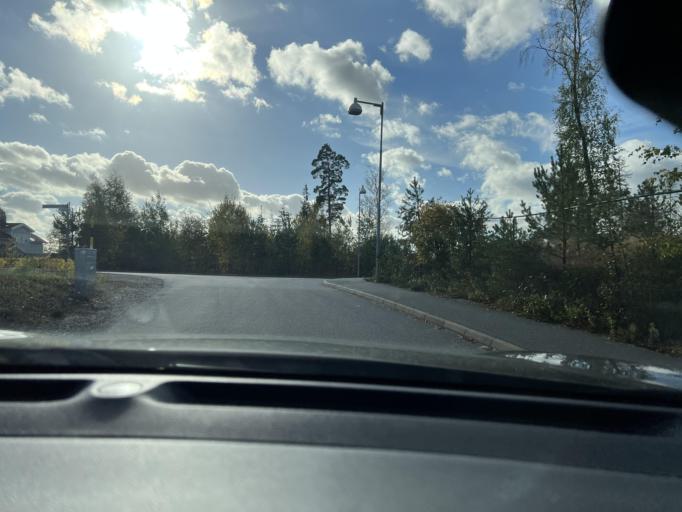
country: SE
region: Stockholm
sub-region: Vallentuna Kommun
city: Vallentuna
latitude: 59.5045
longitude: 18.0805
